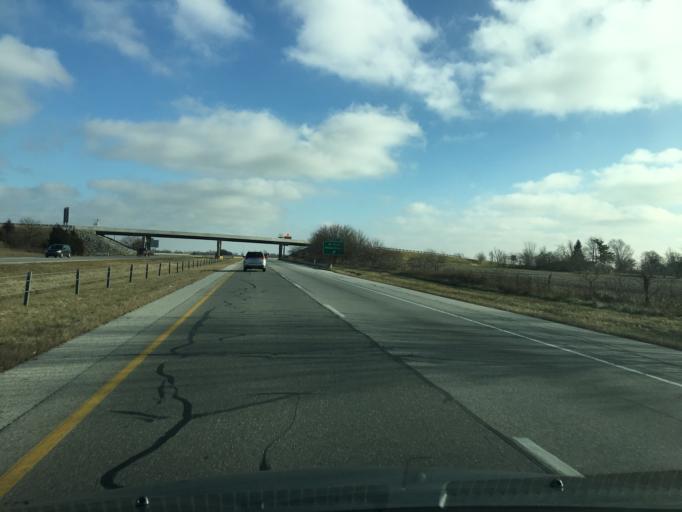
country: US
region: Indiana
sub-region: Decatur County
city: Saint Paul
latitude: 39.4542
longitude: -85.6318
